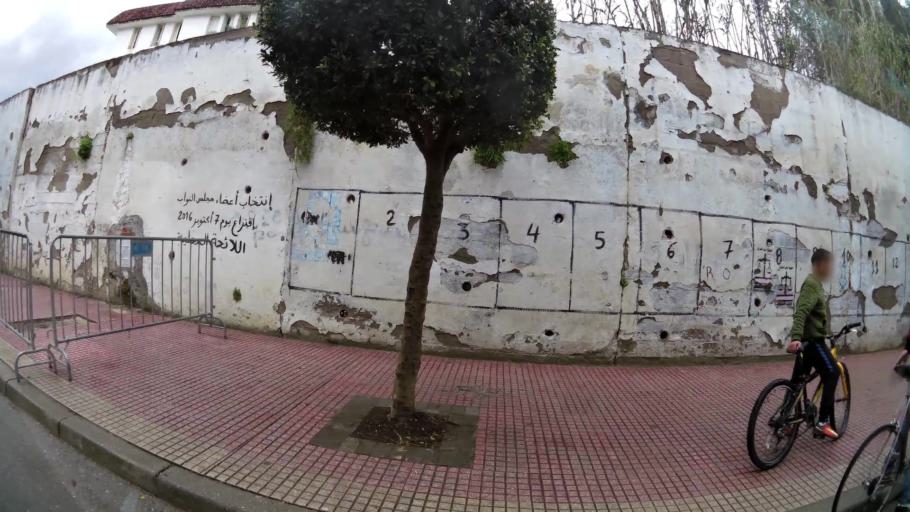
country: MA
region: Tanger-Tetouan
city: Chefchaouene
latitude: 35.1682
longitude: -5.2718
